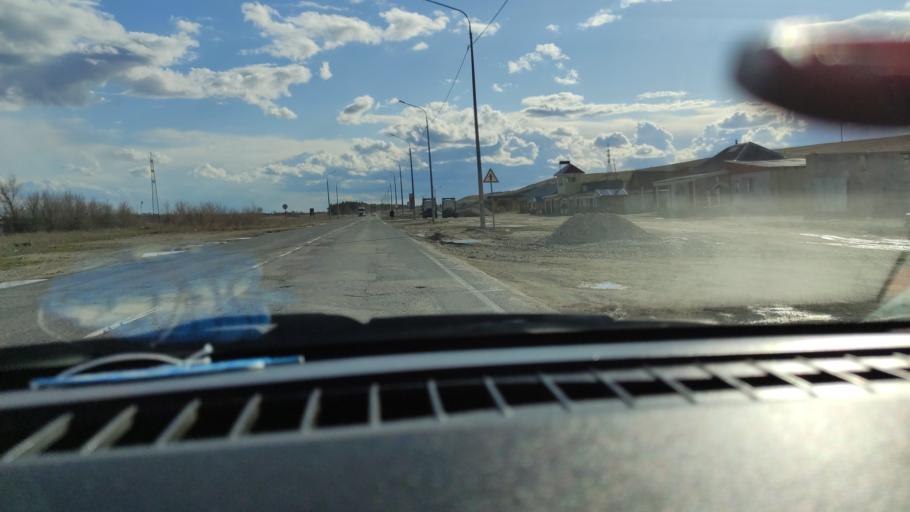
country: RU
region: Saratov
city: Sinodskoye
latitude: 52.0803
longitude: 46.7946
